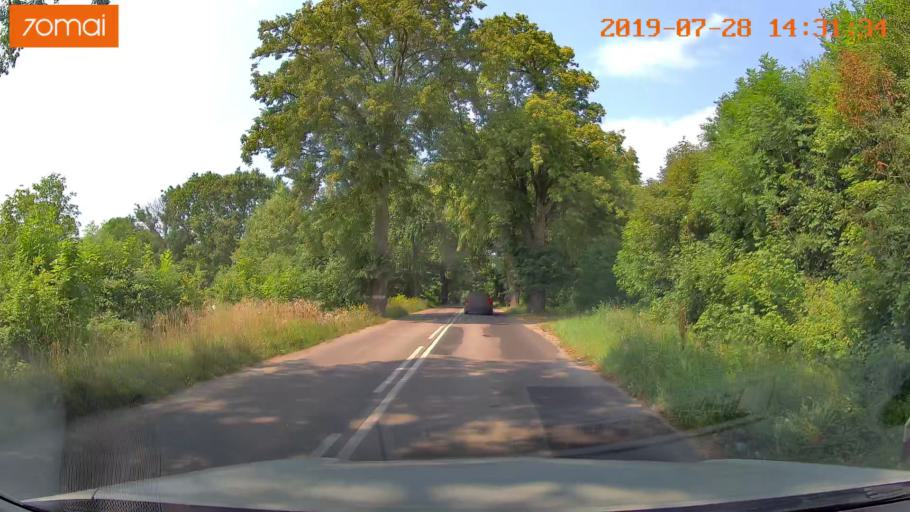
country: RU
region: Kaliningrad
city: Primorsk
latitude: 54.8073
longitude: 20.0502
